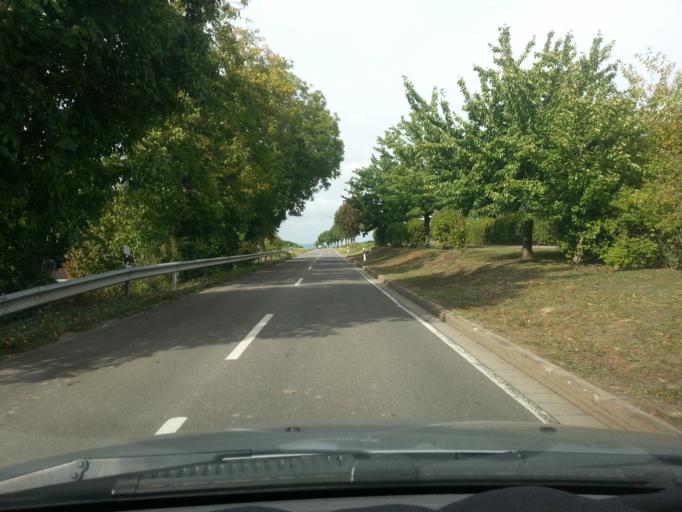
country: DE
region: Rheinland-Pfalz
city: Venningen
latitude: 49.2849
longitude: 8.1735
